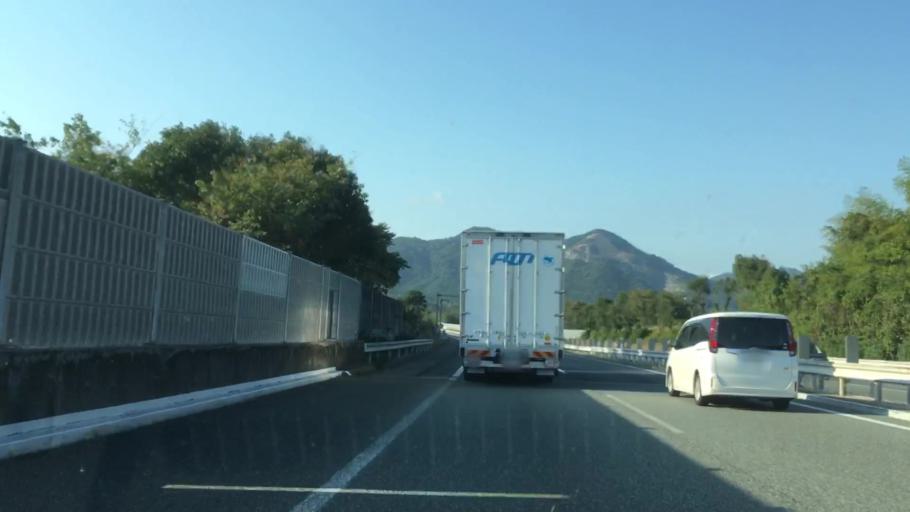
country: JP
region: Yamaguchi
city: Hofu
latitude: 34.0661
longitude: 131.5007
